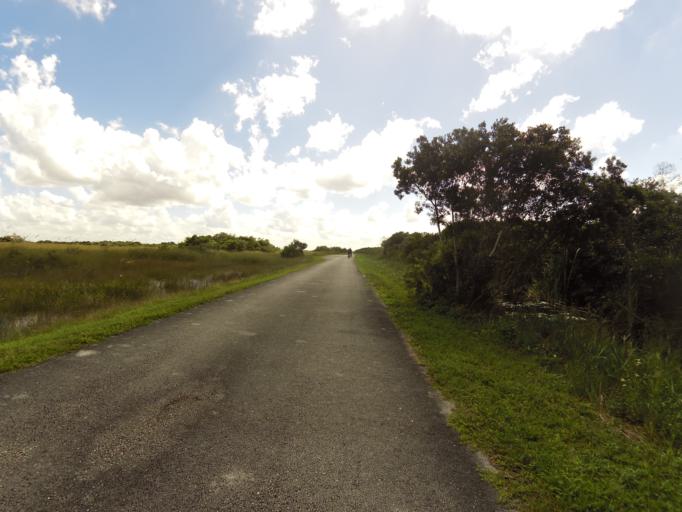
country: US
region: Florida
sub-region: Miami-Dade County
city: The Hammocks
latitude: 25.7175
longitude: -80.7667
